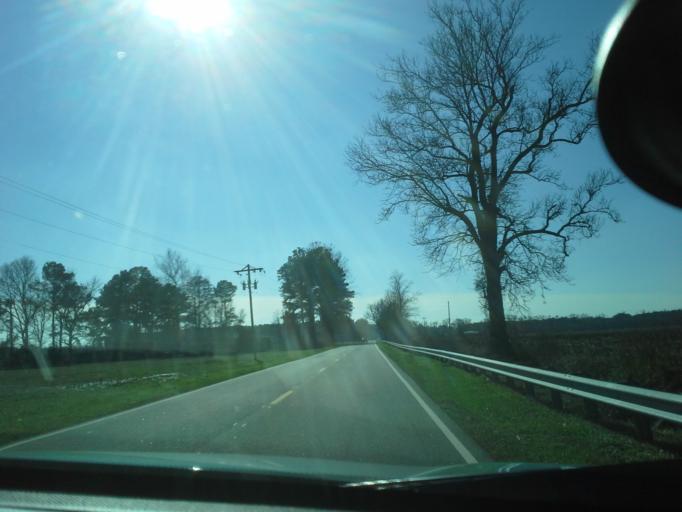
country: US
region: North Carolina
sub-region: Beaufort County
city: Belhaven
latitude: 35.6055
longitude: -76.6589
